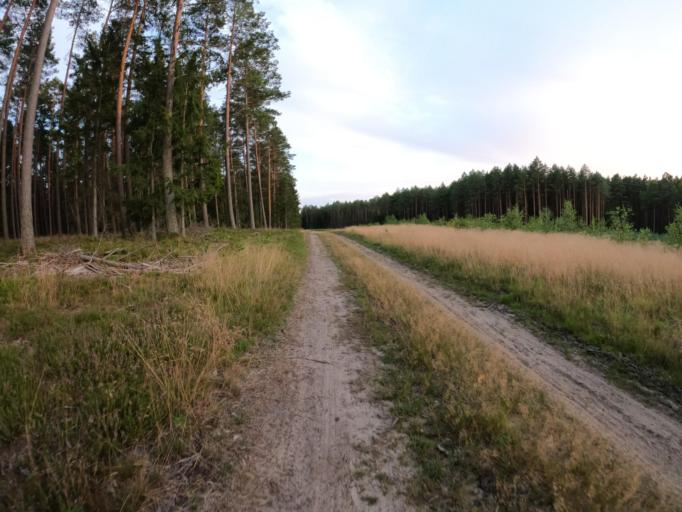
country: PL
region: West Pomeranian Voivodeship
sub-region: Powiat koszalinski
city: Sianow
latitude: 54.0985
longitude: 16.4111
